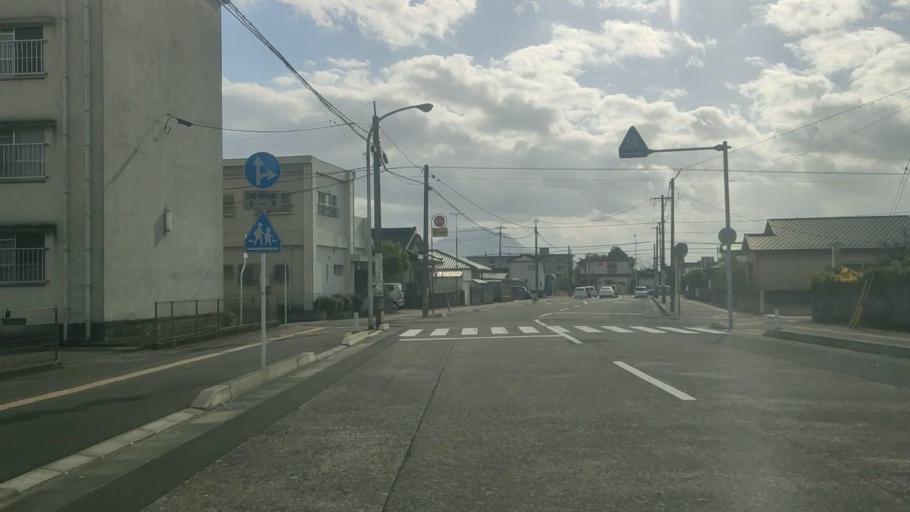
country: JP
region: Kagoshima
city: Kajiki
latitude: 31.7359
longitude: 130.6701
